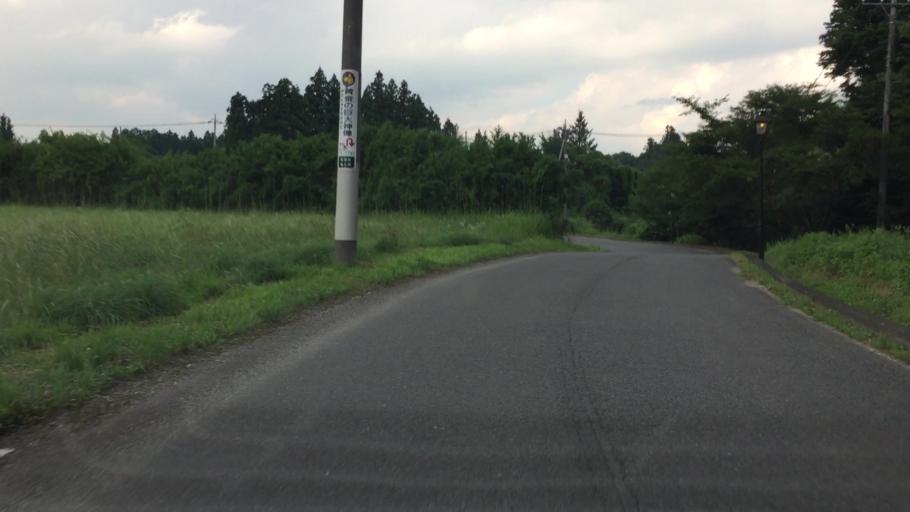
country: JP
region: Tochigi
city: Kuroiso
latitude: 37.0464
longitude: 140.0287
